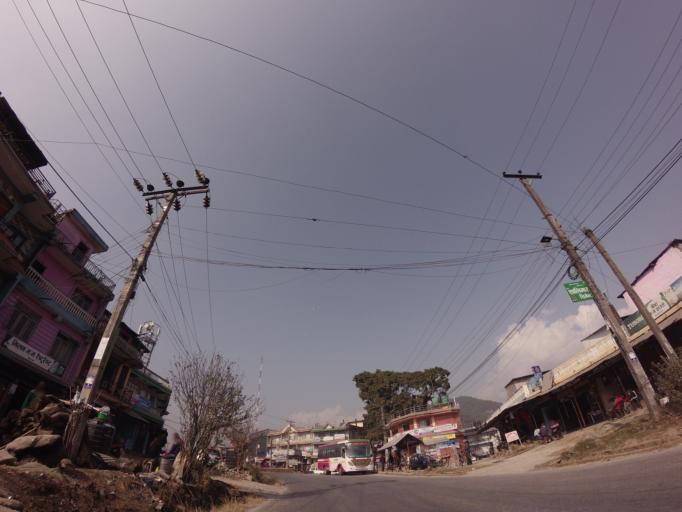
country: NP
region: Western Region
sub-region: Gandaki Zone
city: Pokhara
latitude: 28.2777
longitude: 83.9368
